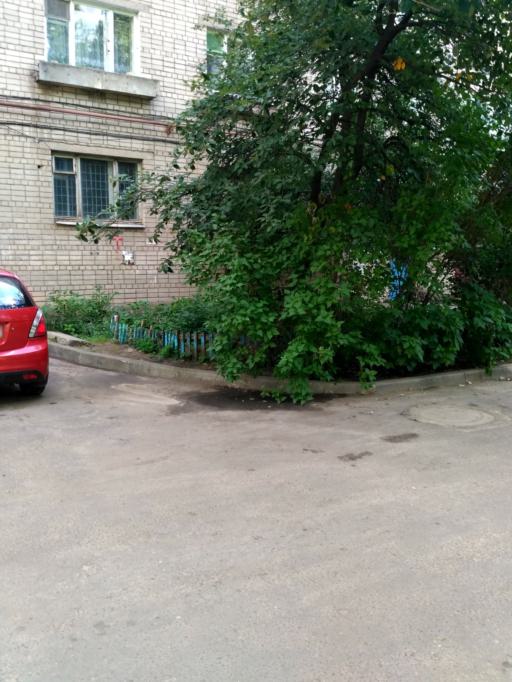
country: RU
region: Voronezj
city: Pridonskoy
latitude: 51.6487
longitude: 39.1209
